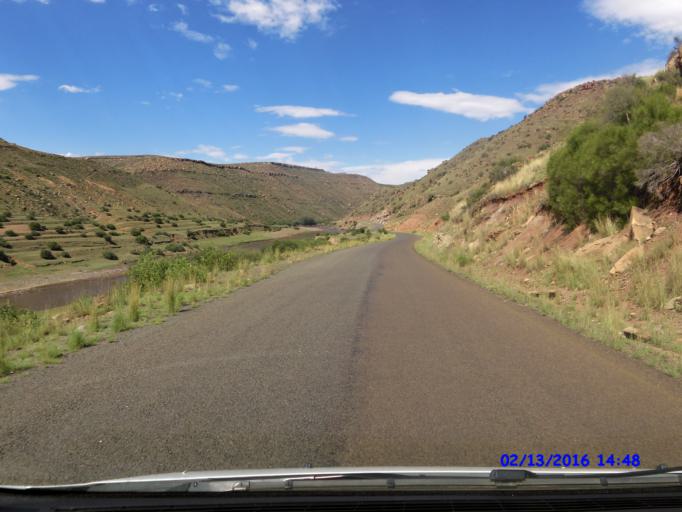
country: LS
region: Qacha's Nek
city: Qacha's Nek
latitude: -30.0683
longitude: 28.4161
